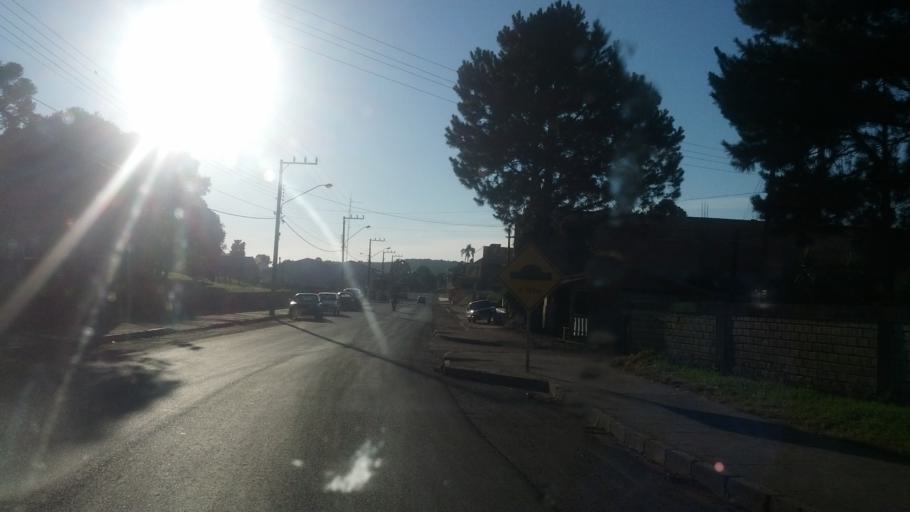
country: BR
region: Rio Grande do Sul
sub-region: Vacaria
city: Estrela
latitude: -27.8972
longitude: -50.7624
